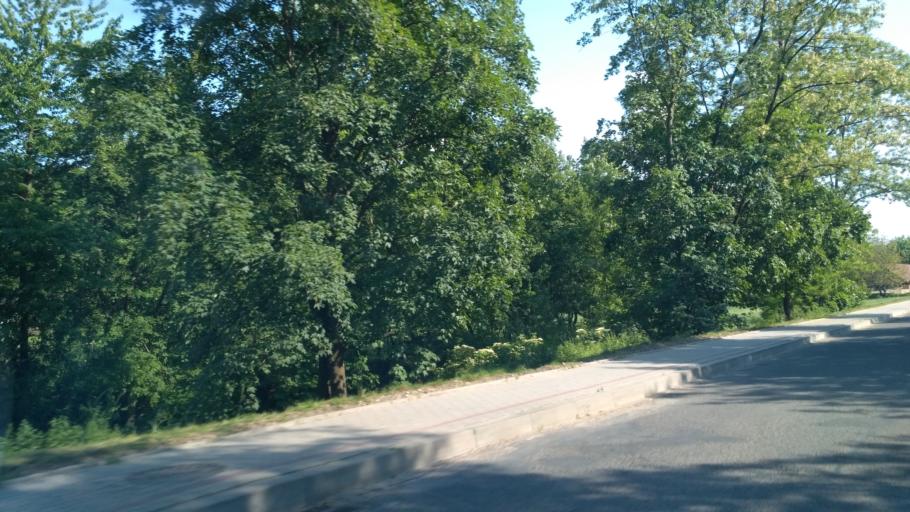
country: PL
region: Subcarpathian Voivodeship
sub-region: Powiat jaroslawski
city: Pruchnik
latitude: 49.8897
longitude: 22.4979
